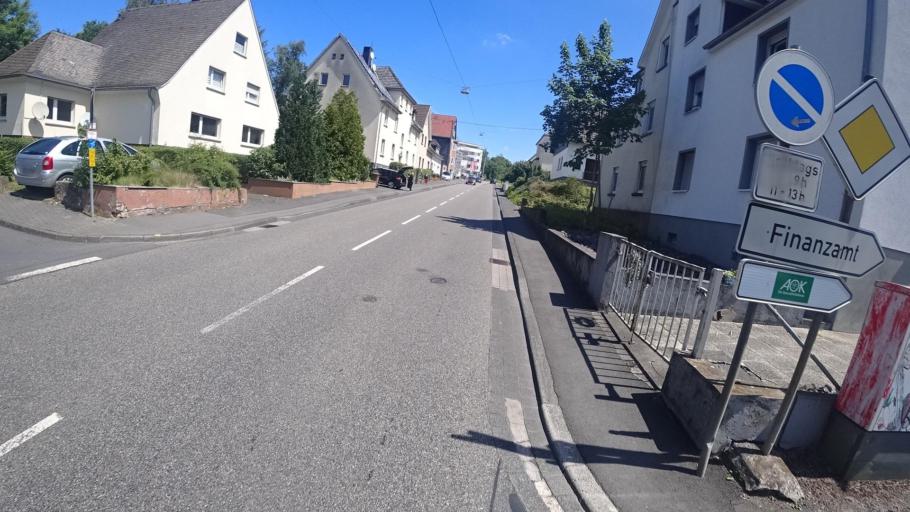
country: DE
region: Rheinland-Pfalz
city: Altenkirchen
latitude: 50.6893
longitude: 7.6526
